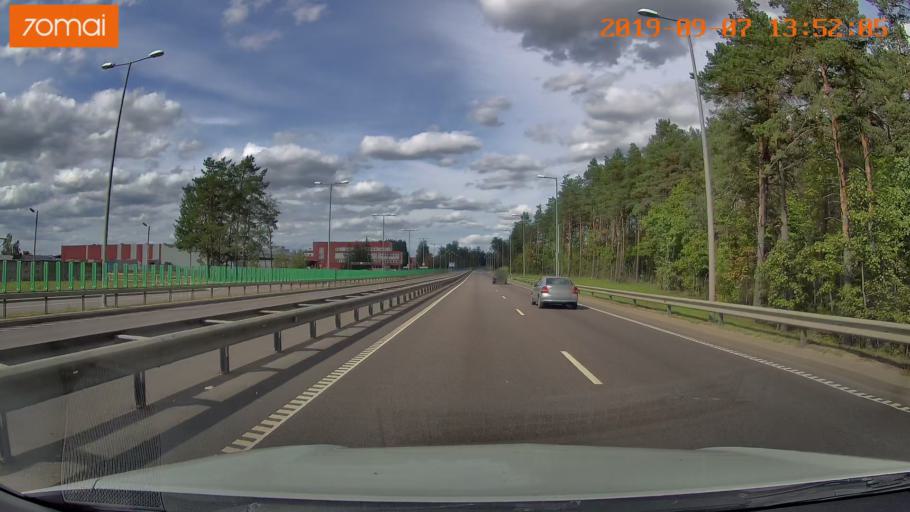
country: LT
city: Baltoji Voke
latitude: 54.6228
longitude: 25.1554
